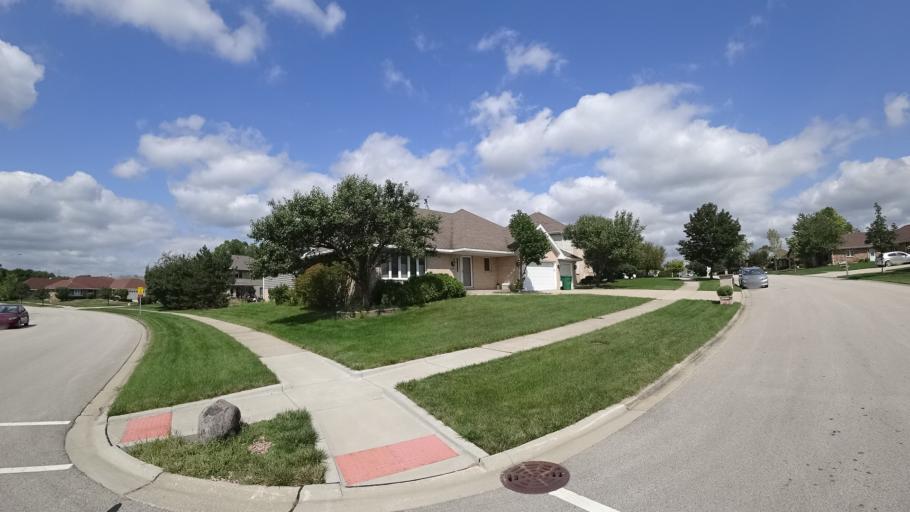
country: US
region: Illinois
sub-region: Will County
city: Mokena
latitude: 41.5610
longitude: -87.8730
